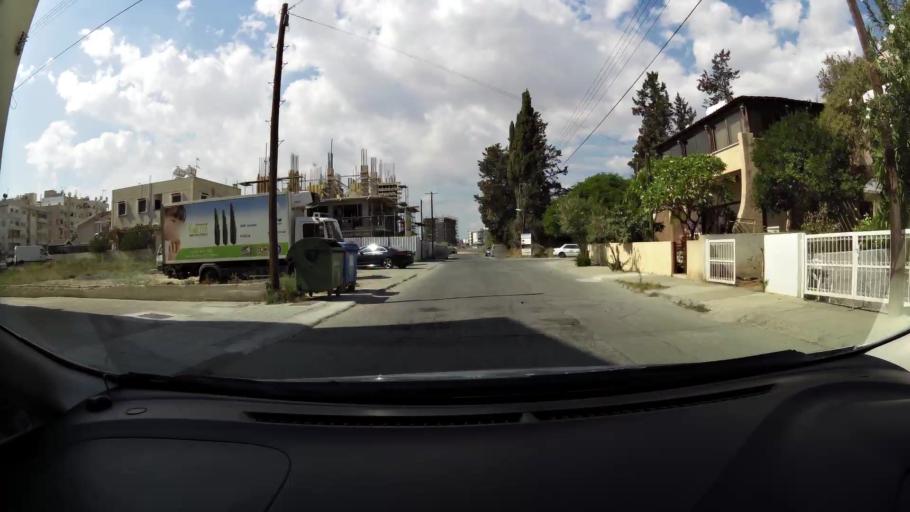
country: CY
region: Larnaka
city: Larnaca
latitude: 34.9097
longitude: 33.6272
